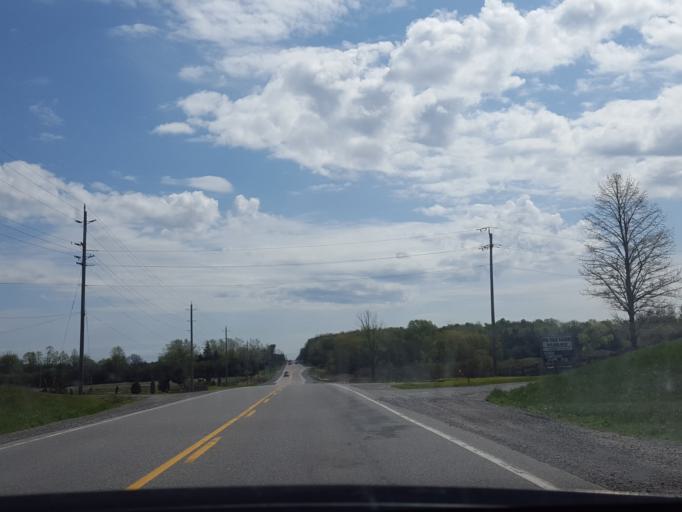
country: CA
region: Ontario
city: Oshawa
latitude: 44.1096
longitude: -78.8653
